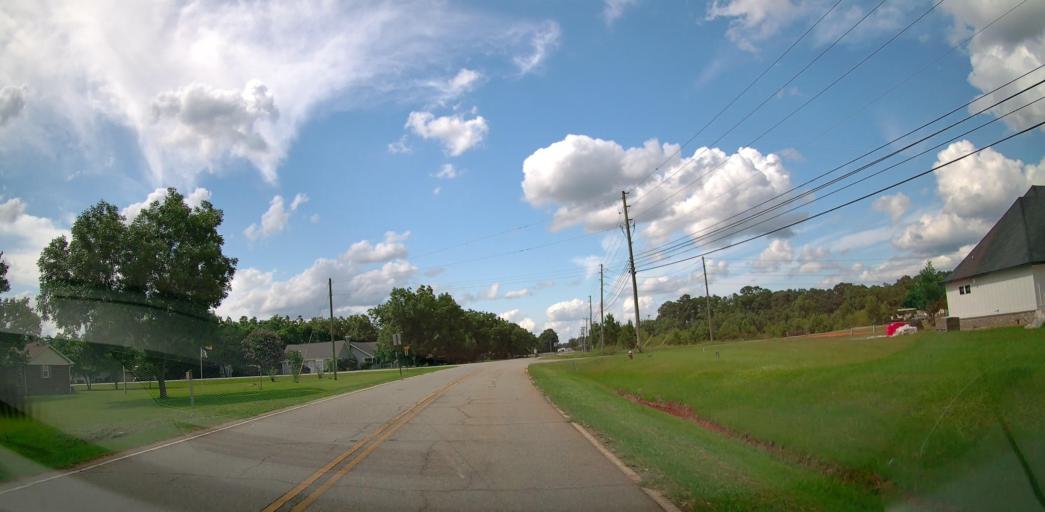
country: US
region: Georgia
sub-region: Houston County
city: Centerville
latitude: 32.5833
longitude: -83.6663
